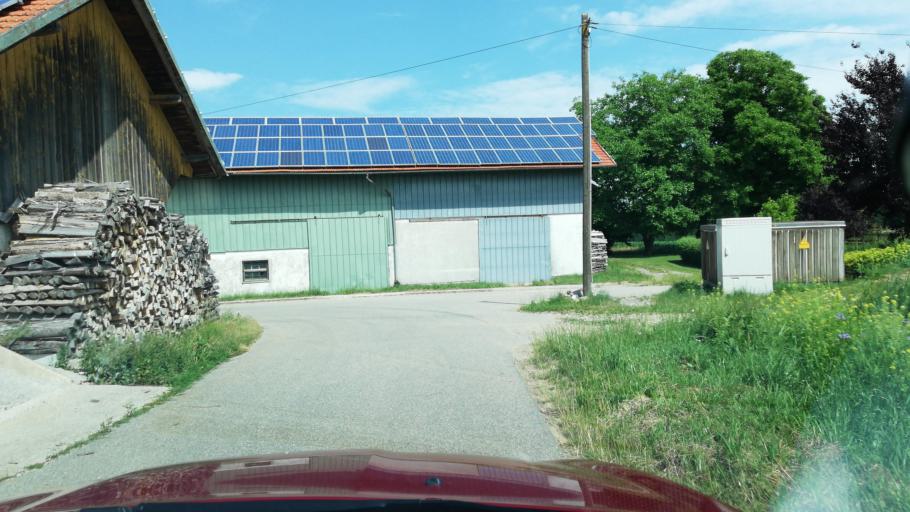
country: DE
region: Bavaria
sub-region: Upper Bavaria
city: Tacherting
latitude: 48.0703
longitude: 12.5965
